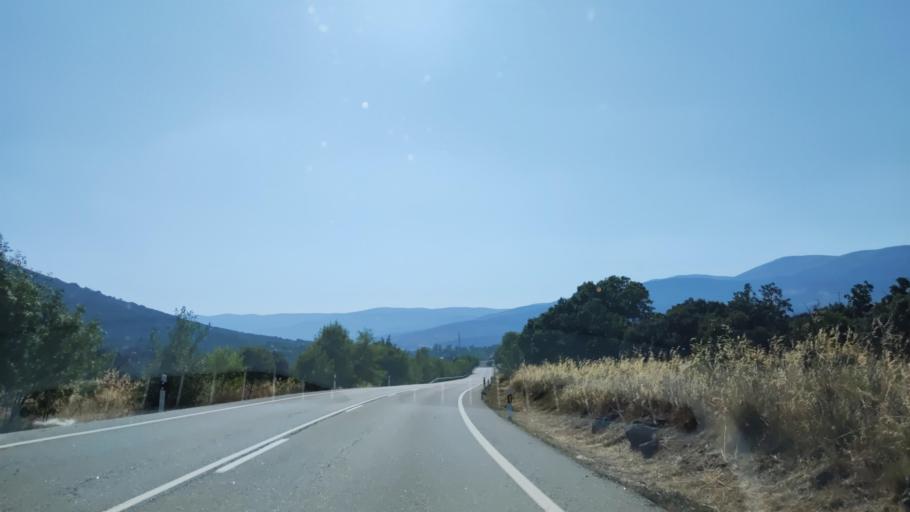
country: ES
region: Madrid
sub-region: Provincia de Madrid
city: Lozoya
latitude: 40.9467
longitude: -3.7548
